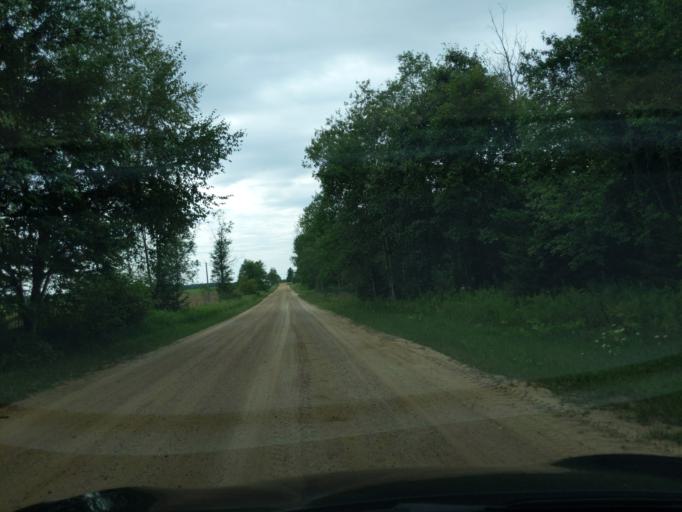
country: US
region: Michigan
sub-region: Clare County
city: Harrison
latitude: 44.0025
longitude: -84.9829
